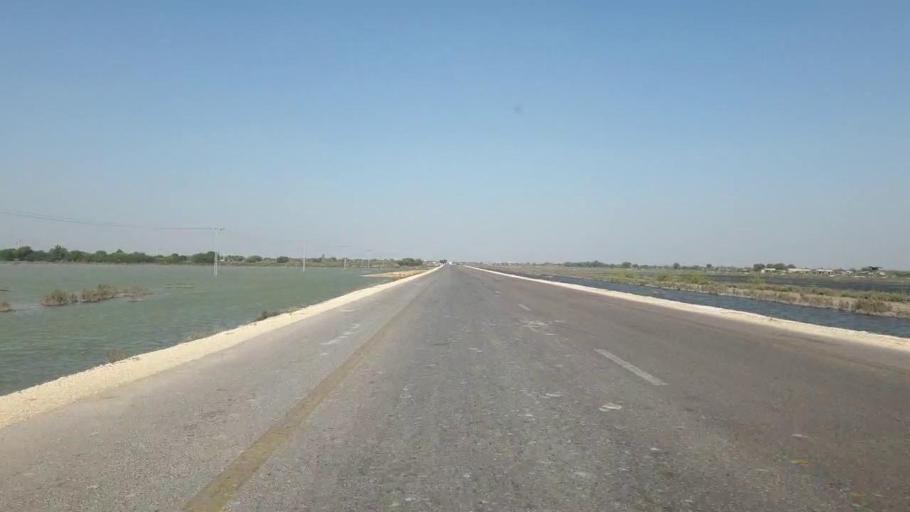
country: PK
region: Sindh
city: Talhar
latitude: 24.8373
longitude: 68.8161
